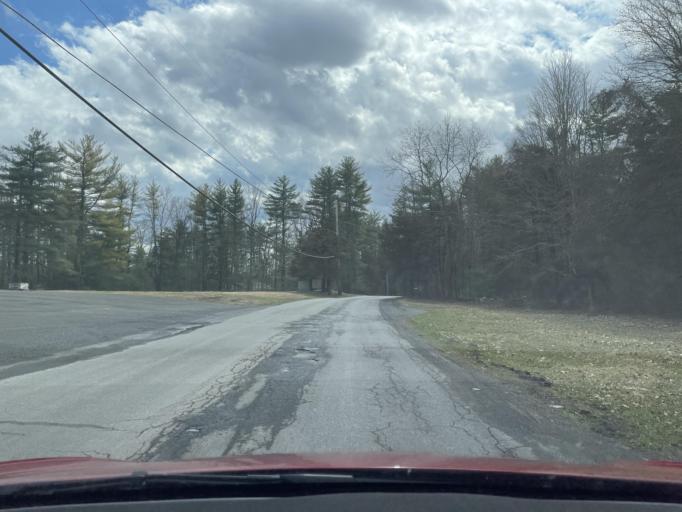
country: US
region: New York
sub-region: Ulster County
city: Zena
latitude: 42.0445
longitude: -74.0286
